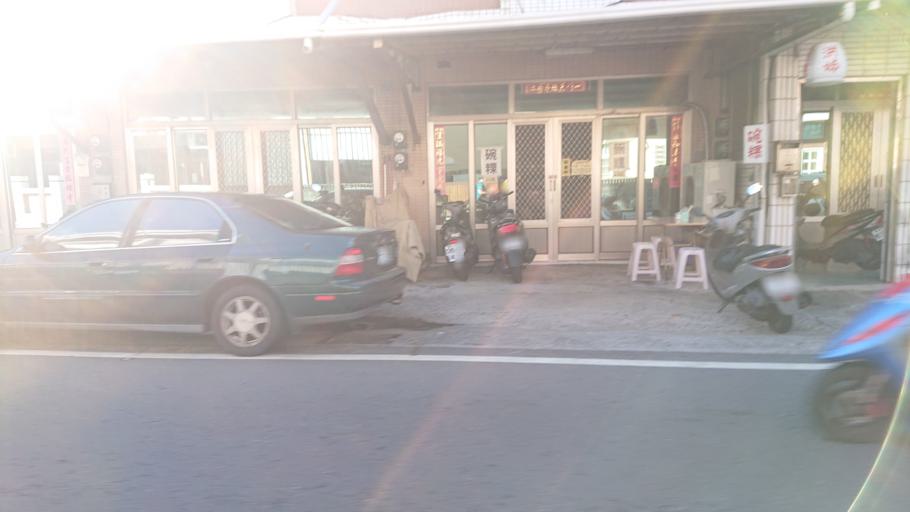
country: TW
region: Taiwan
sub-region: Penghu
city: Ma-kung
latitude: 23.5782
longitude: 119.5776
